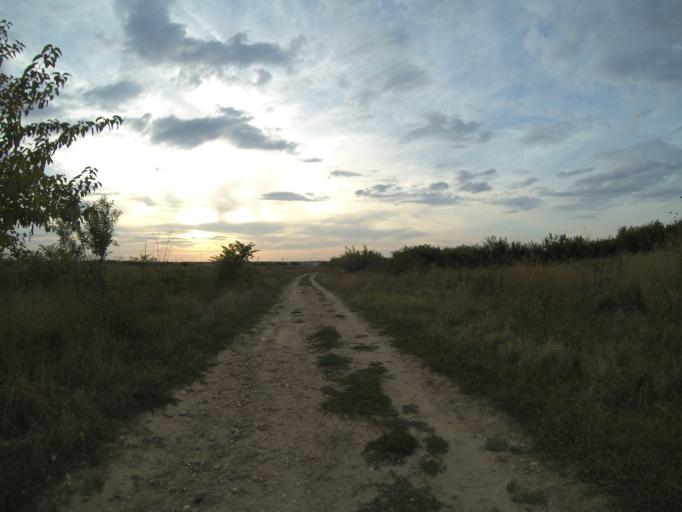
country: RO
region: Dolj
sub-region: Comuna Ceratu
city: Ceratu
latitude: 44.0872
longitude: 23.6711
